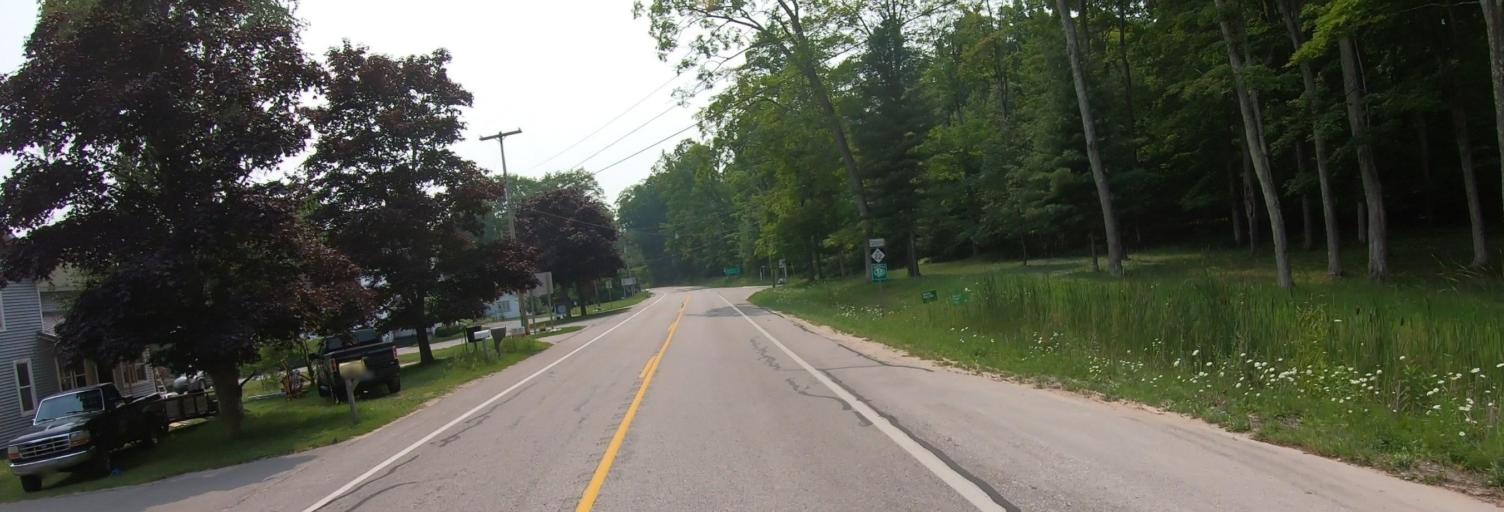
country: US
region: Michigan
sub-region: Leelanau County
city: Leland
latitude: 45.1245
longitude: -85.6180
